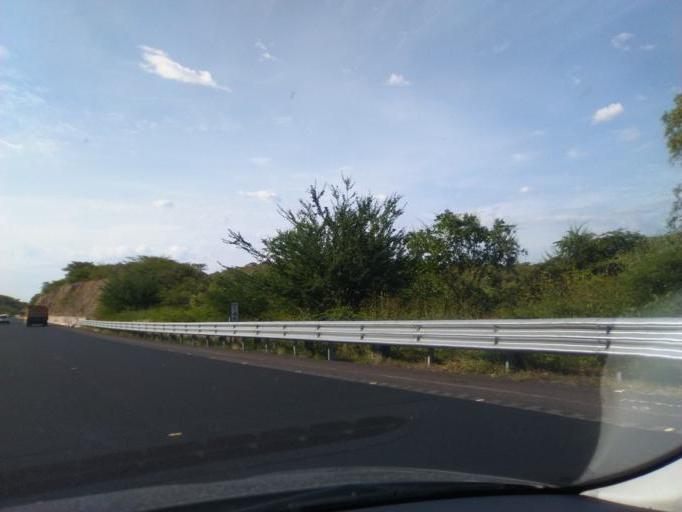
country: MX
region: Morelos
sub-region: Jojutla
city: Higueron
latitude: 18.4975
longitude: -99.1869
